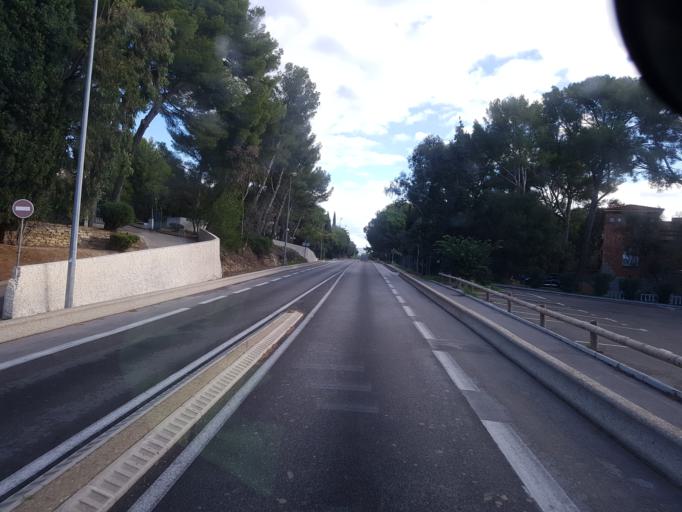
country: FR
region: Provence-Alpes-Cote d'Azur
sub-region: Departement du Var
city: Saint-Cyr-sur-Mer
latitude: 43.1803
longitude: 5.6803
